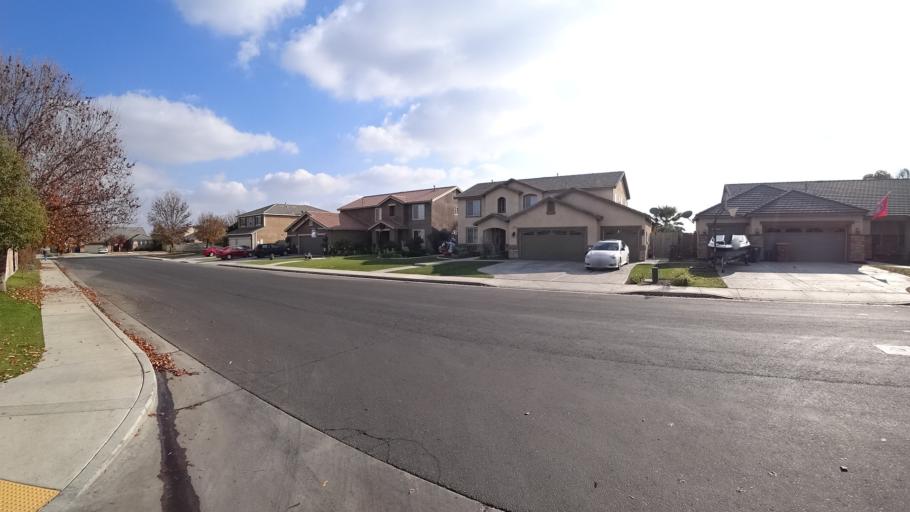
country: US
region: California
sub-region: Kern County
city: Greenacres
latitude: 35.3003
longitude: -119.1056
